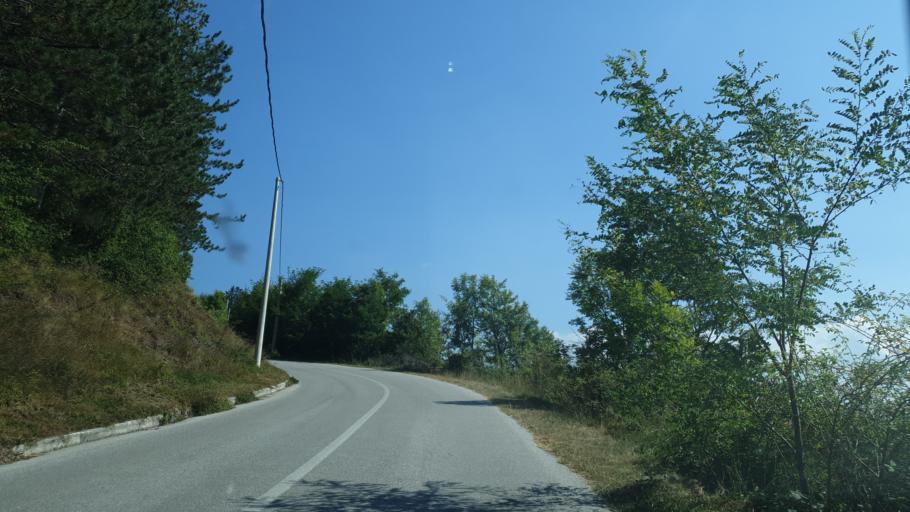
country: RS
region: Central Serbia
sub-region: Zlatiborski Okrug
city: Cajetina
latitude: 43.6762
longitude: 19.8320
